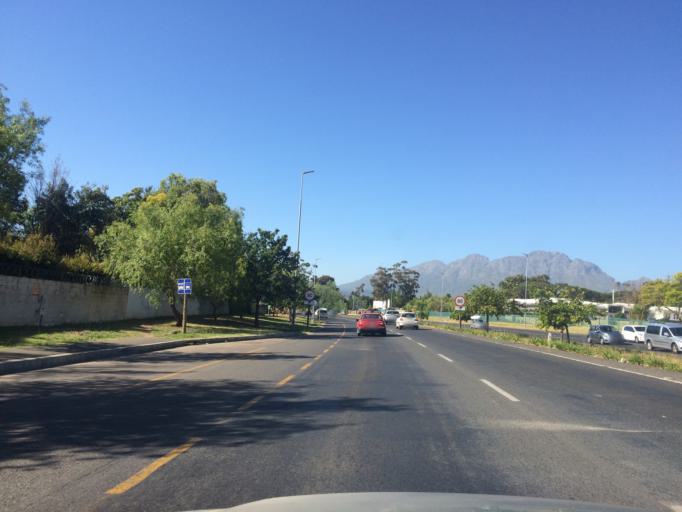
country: ZA
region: Western Cape
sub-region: Cape Winelands District Municipality
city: Stellenbosch
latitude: -33.9565
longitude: 18.8550
